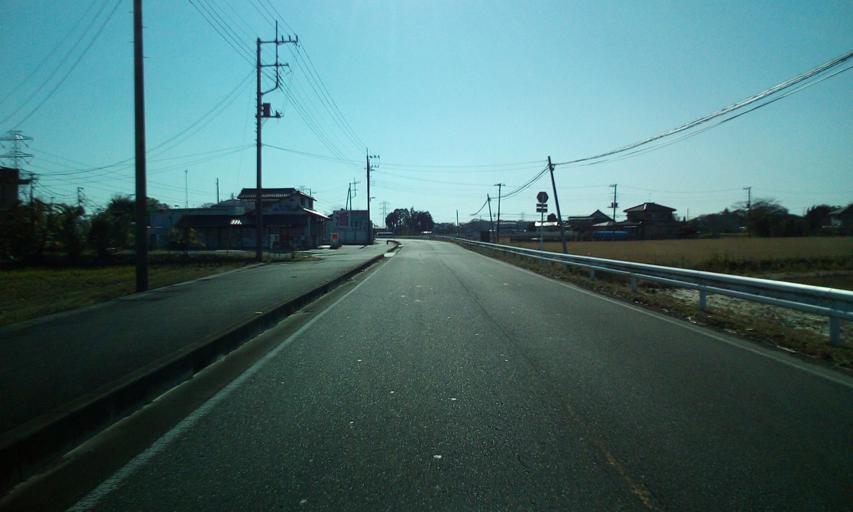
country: JP
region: Ibaraki
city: Sakai
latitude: 36.0570
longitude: 139.7778
